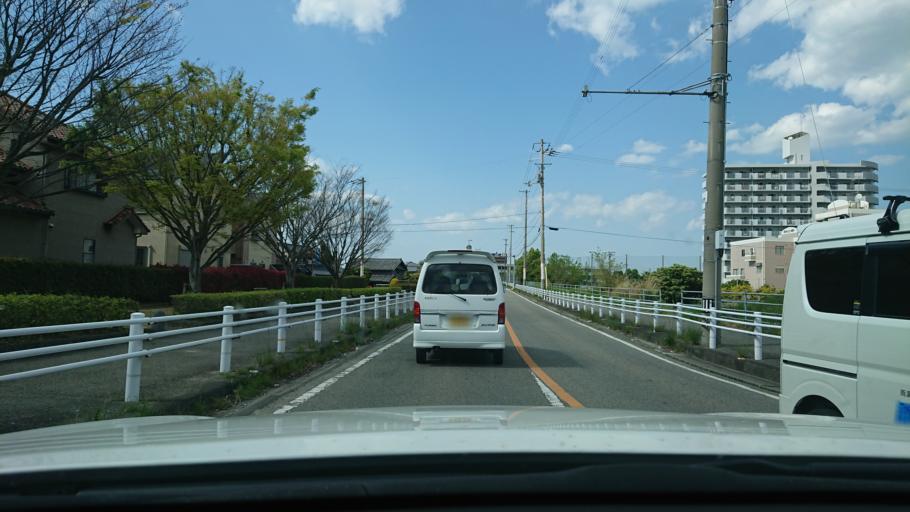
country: JP
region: Tokushima
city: Komatsushimacho
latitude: 34.0140
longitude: 134.5558
